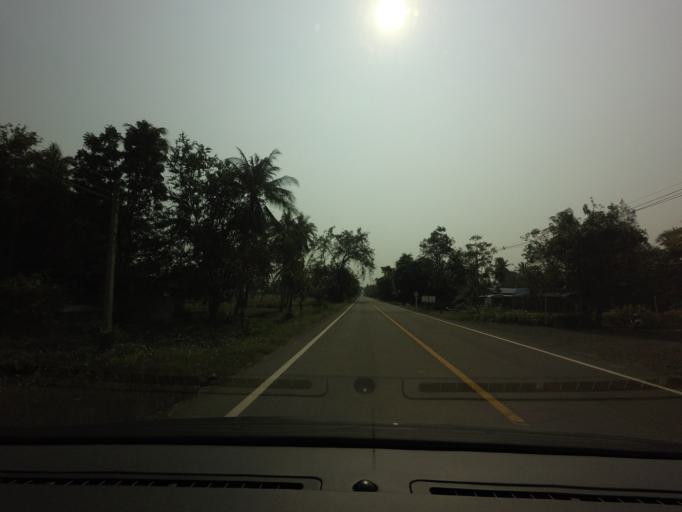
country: TH
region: Prachuap Khiri Khan
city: Kui Buri
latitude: 12.0254
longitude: 99.8902
